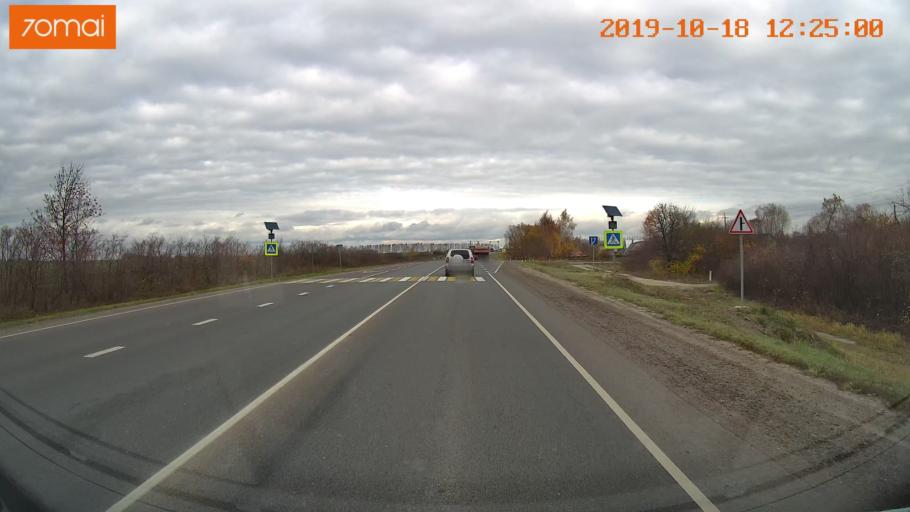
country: RU
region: Rjazan
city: Rybnoye
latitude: 54.5449
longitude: 39.5163
